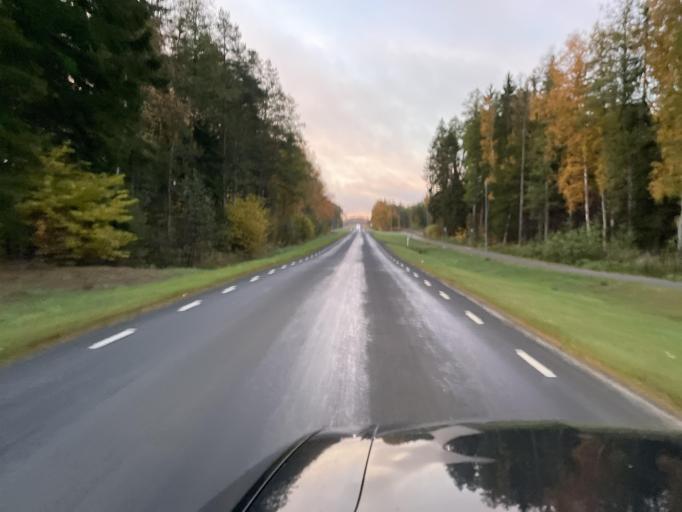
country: EE
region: Harju
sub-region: Nissi vald
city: Riisipere
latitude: 59.2453
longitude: 24.2425
